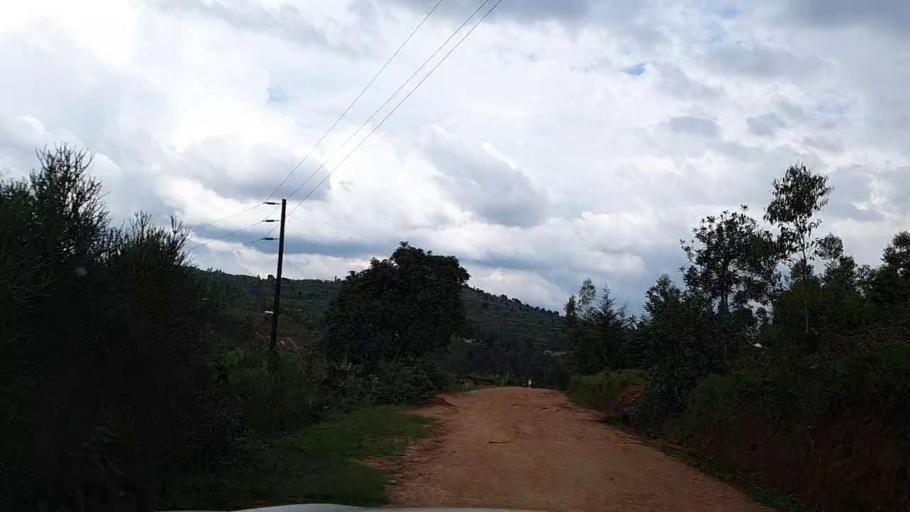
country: RW
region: Southern Province
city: Gikongoro
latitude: -2.4165
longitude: 29.6561
